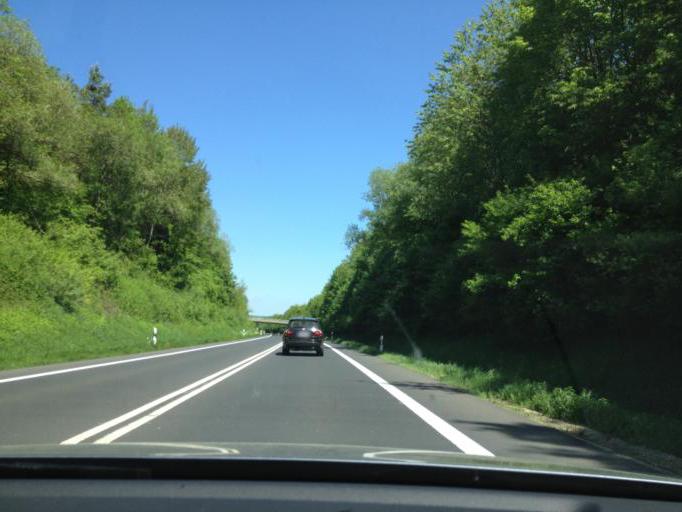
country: DE
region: Rheinland-Pfalz
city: Fliessem
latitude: 50.0029
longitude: 6.5375
